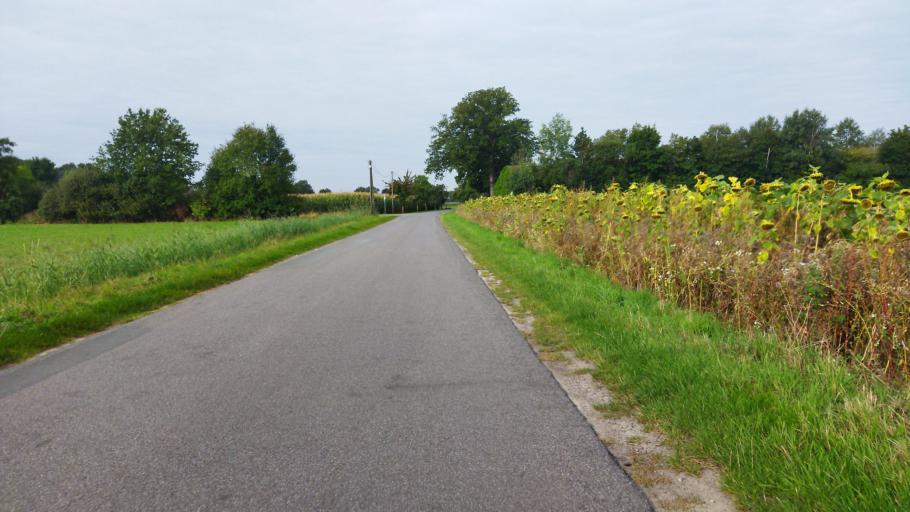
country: DE
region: Lower Saxony
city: Bad Laer
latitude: 52.0798
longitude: 8.1083
